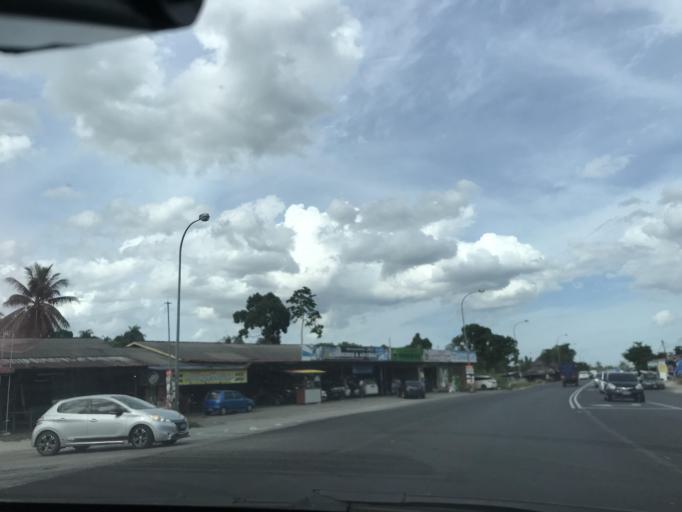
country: MY
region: Kelantan
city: Kampung Lemal
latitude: 6.0346
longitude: 102.1529
